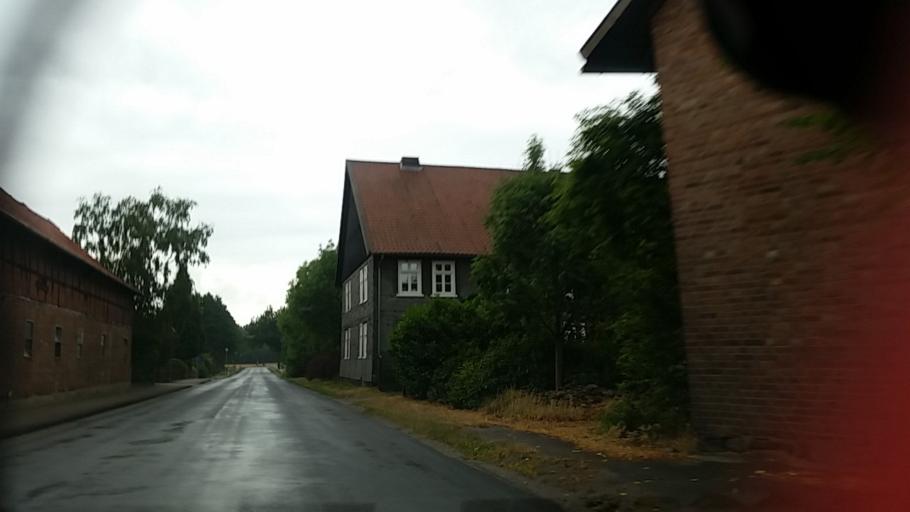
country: DE
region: Lower Saxony
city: Bokensdorf
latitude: 52.4963
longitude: 10.7131
